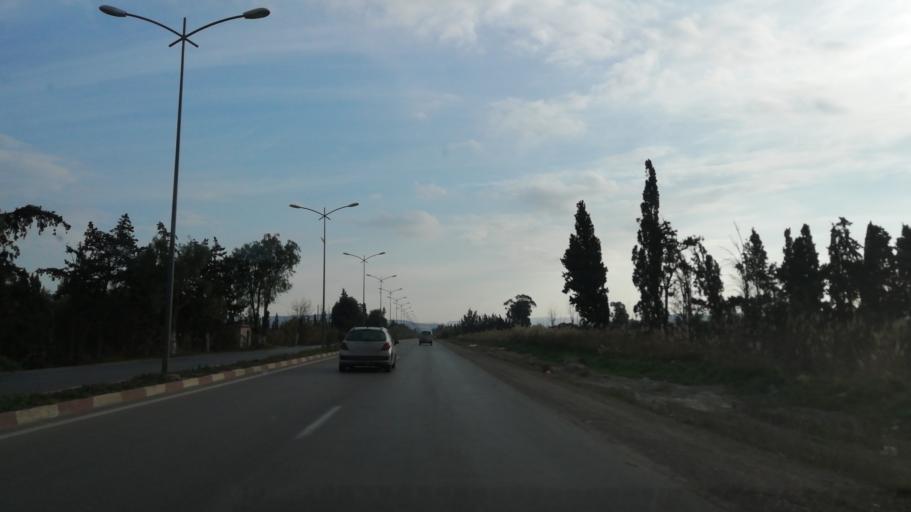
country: DZ
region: Mascara
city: Mascara
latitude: 35.6216
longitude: 0.0619
